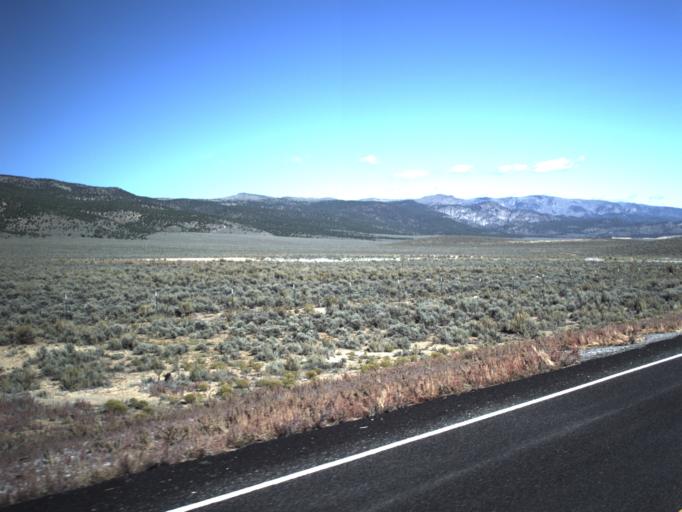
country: US
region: Utah
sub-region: Piute County
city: Junction
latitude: 38.2303
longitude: -111.9956
